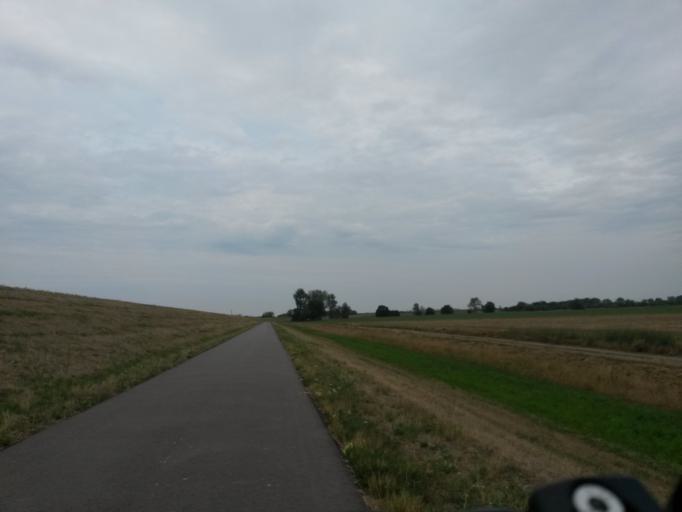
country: DE
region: Saxony-Anhalt
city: Tangermunde
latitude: 52.5479
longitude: 12.0030
